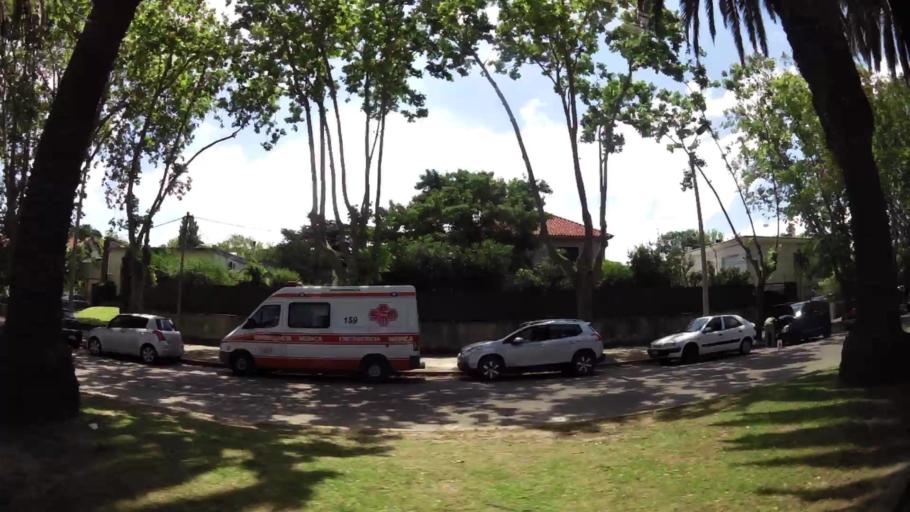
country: UY
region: Montevideo
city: Montevideo
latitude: -34.8695
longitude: -56.2034
